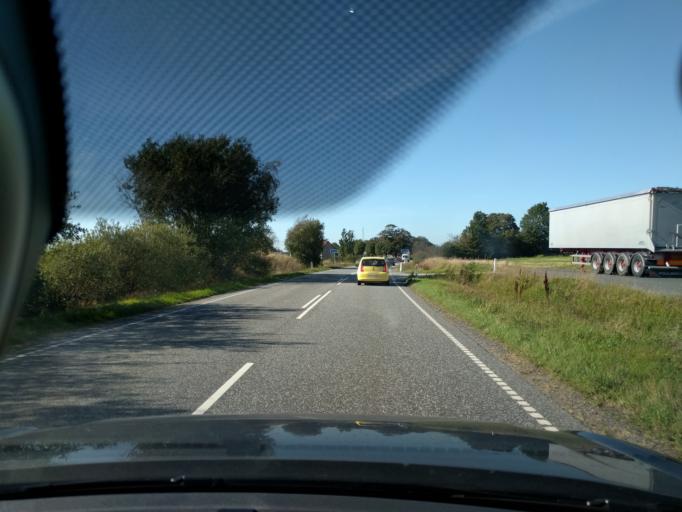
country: DK
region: North Denmark
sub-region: Mariagerfjord Kommune
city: Hobro
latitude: 56.6736
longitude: 9.6806
